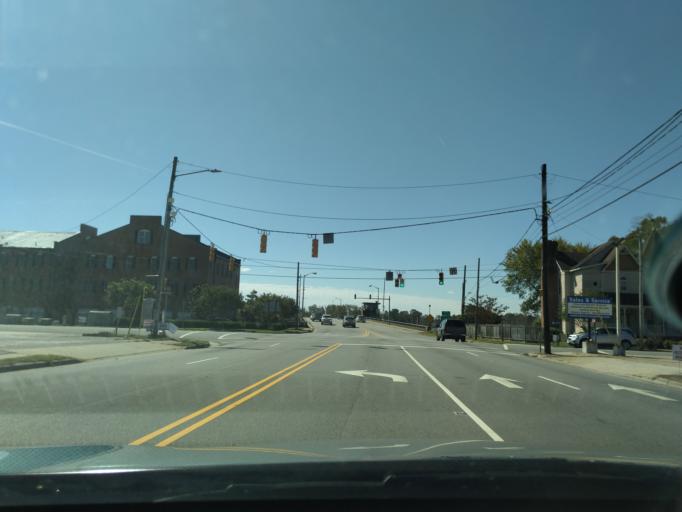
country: US
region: North Carolina
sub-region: Beaufort County
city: Washington
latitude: 35.5451
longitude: -77.0607
